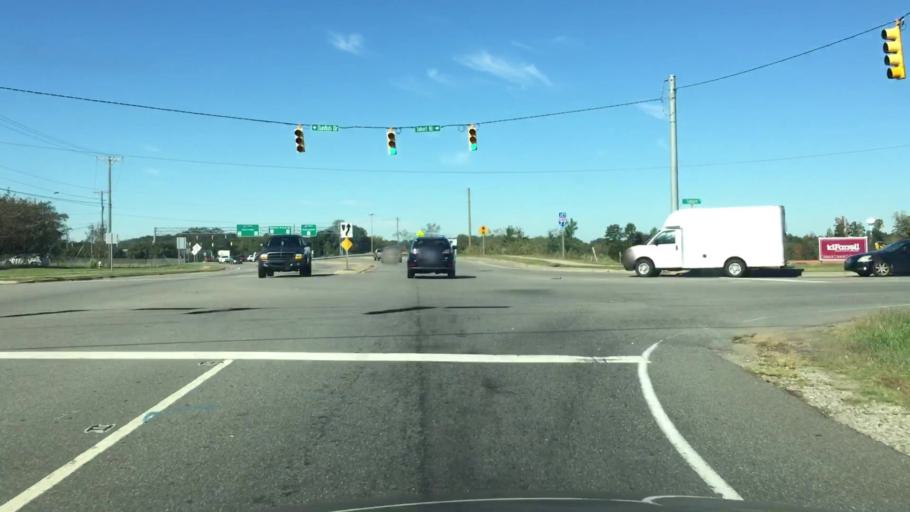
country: US
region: North Carolina
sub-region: Iredell County
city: Mooresville
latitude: 35.5795
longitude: -80.8529
